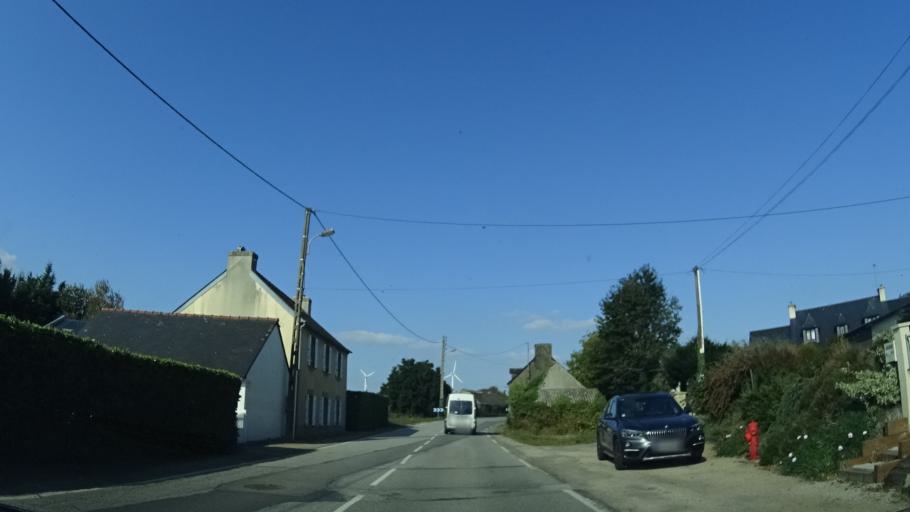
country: FR
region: Brittany
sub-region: Departement du Finistere
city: Cast
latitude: 48.1615
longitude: -4.1346
